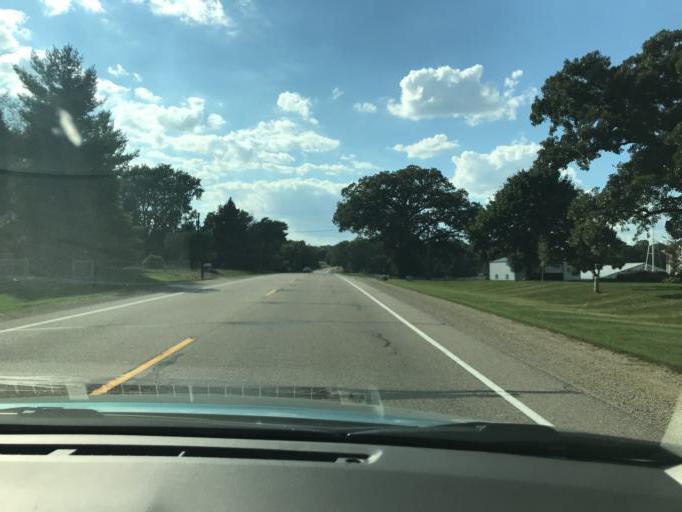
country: US
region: Wisconsin
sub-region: Rock County
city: Orfordville
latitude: 42.5257
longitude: -89.2134
